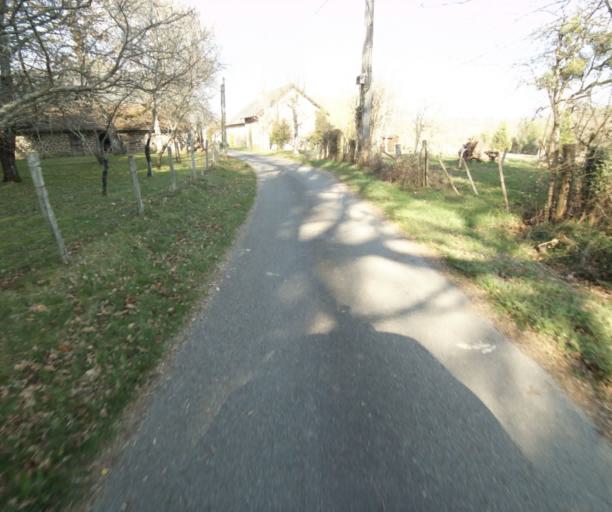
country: FR
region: Limousin
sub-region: Departement de la Correze
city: Saint-Mexant
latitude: 45.3382
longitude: 1.6092
